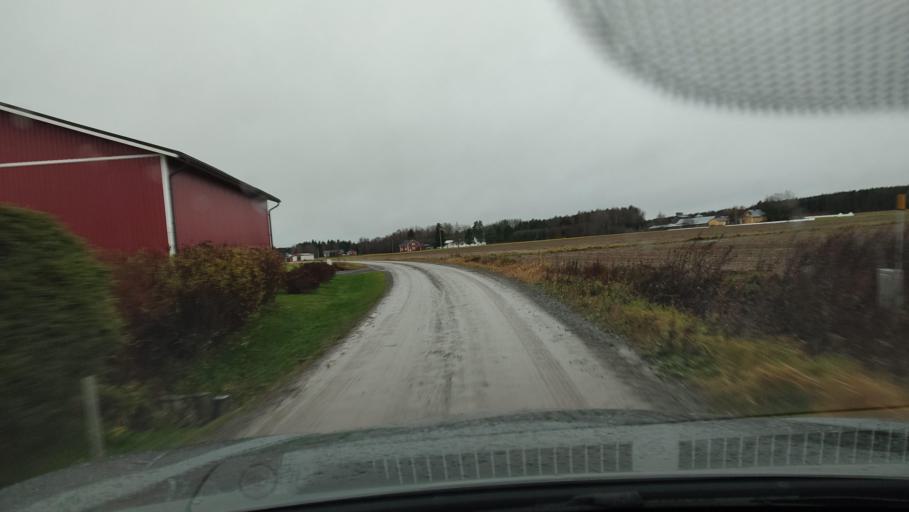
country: FI
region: Southern Ostrobothnia
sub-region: Suupohja
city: Karijoki
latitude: 62.2427
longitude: 21.5520
